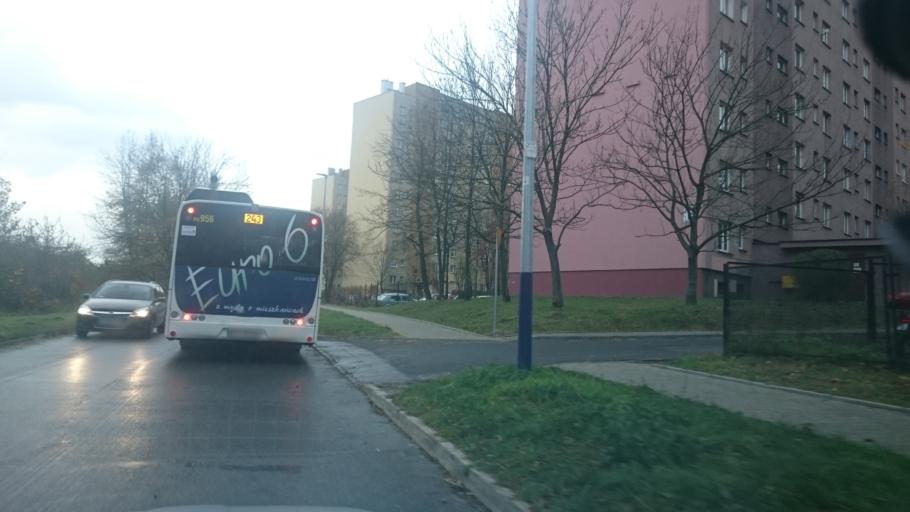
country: PL
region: Lesser Poland Voivodeship
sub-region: Powiat wielicki
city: Czarnochowice
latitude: 50.0193
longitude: 20.0080
